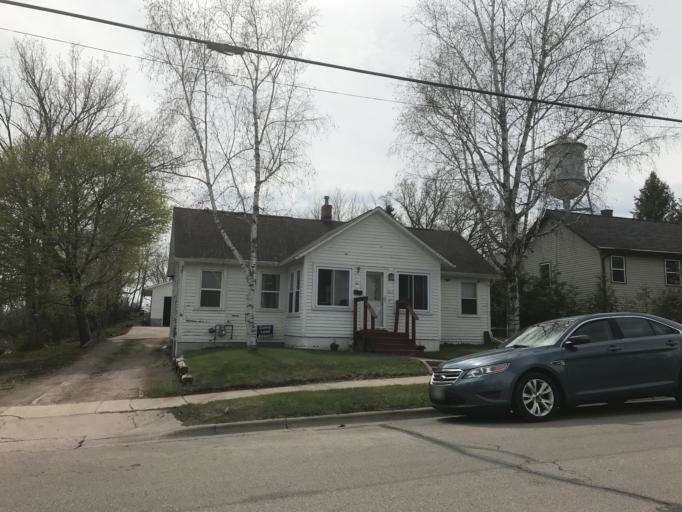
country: US
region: Wisconsin
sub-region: Oconto County
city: Oconto Falls
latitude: 44.8723
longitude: -88.1411
